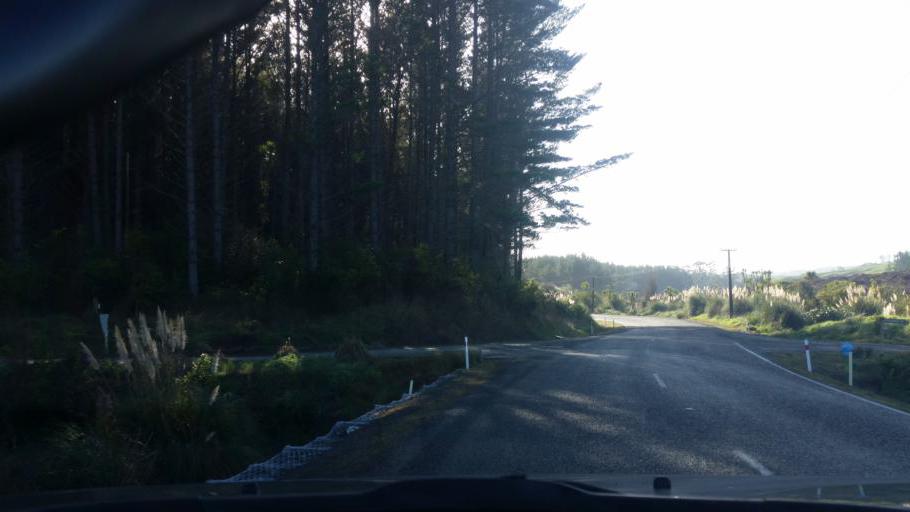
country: NZ
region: Auckland
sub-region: Auckland
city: Wellsford
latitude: -36.2190
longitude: 174.4641
